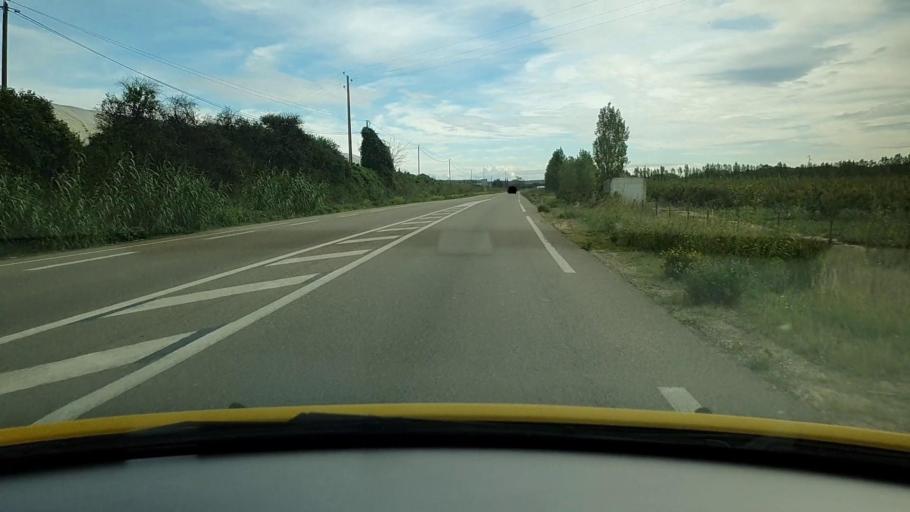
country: FR
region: Languedoc-Roussillon
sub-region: Departement du Gard
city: Bellegarde
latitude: 43.7634
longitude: 4.5265
